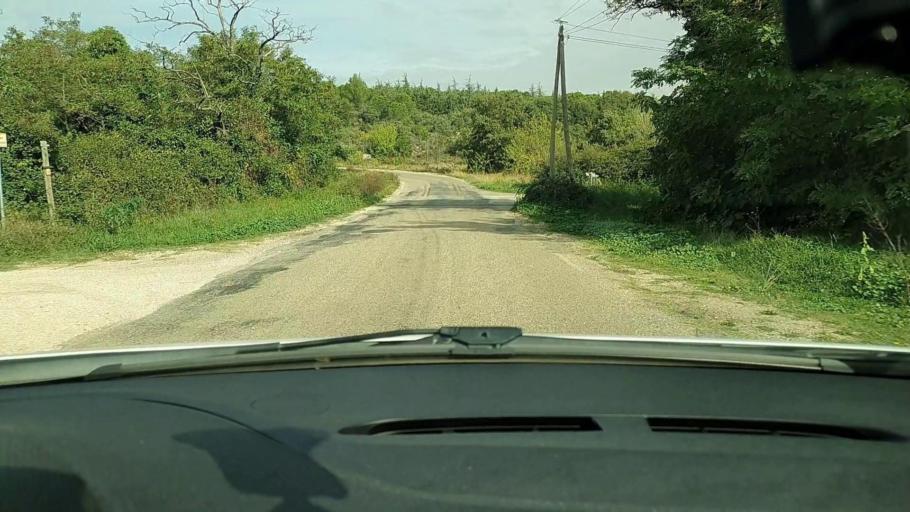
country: FR
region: Languedoc-Roussillon
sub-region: Departement du Gard
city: Saint-Quentin-la-Poterie
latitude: 44.1159
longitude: 4.4149
